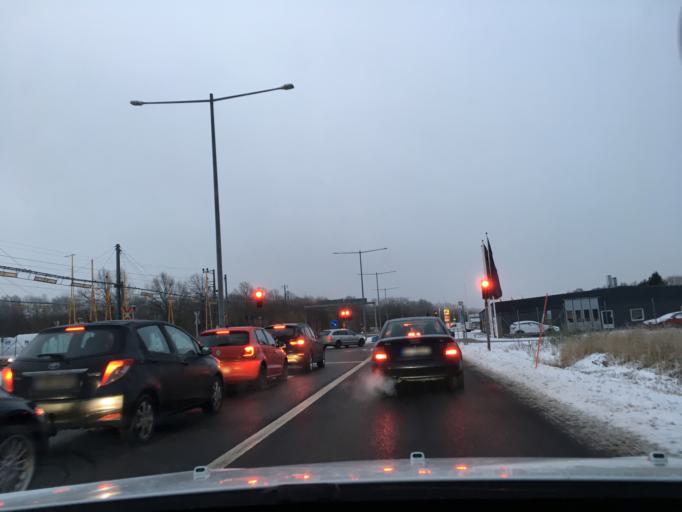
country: SE
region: Vaestra Goetaland
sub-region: Stenungsunds Kommun
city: Stenungsund
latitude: 58.0792
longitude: 11.8294
